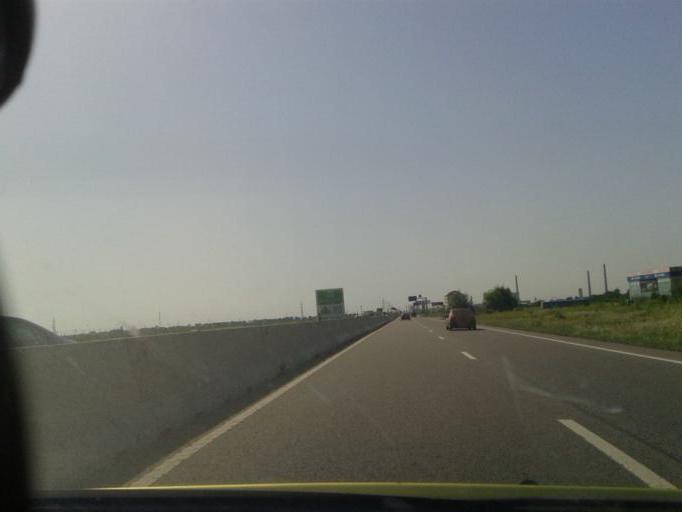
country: RO
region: Prahova
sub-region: Comuna Targsoru Vechi
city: Strejnicu
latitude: 44.9152
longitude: 25.9883
